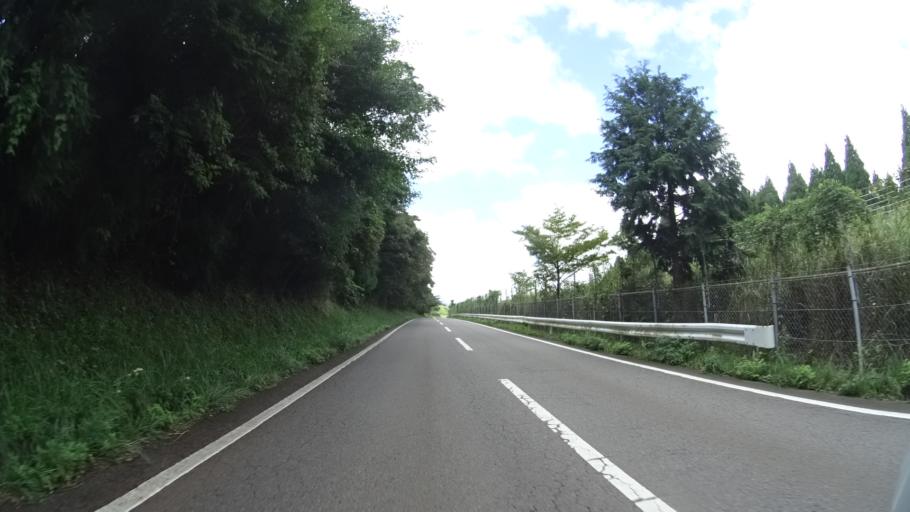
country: JP
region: Oita
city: Beppu
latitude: 33.3331
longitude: 131.4237
